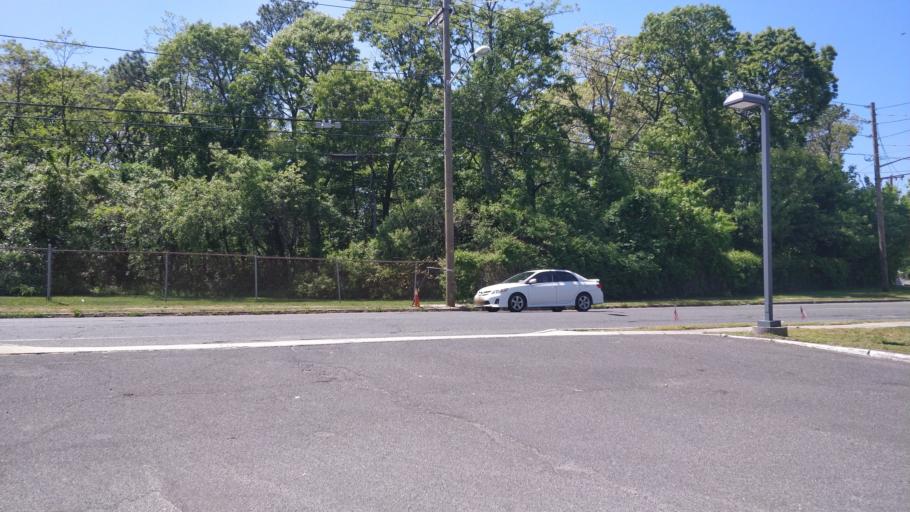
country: US
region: New York
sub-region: Suffolk County
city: Holbrook
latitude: 40.8031
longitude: -73.0691
